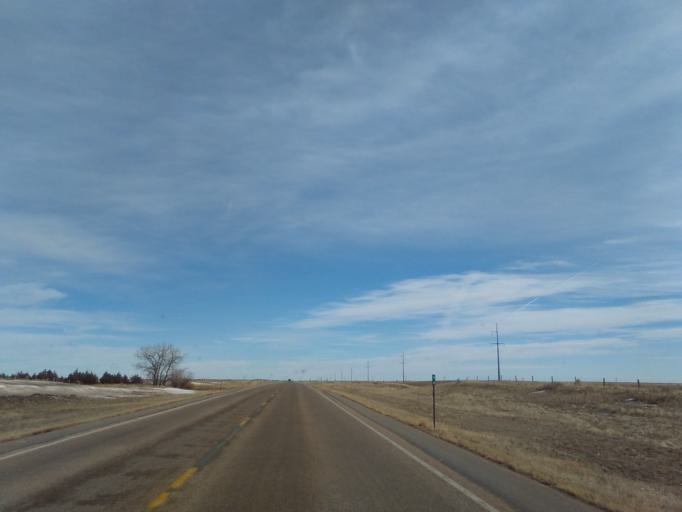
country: US
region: Wyoming
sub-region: Laramie County
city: Pine Bluffs
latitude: 41.4241
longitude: -104.3944
